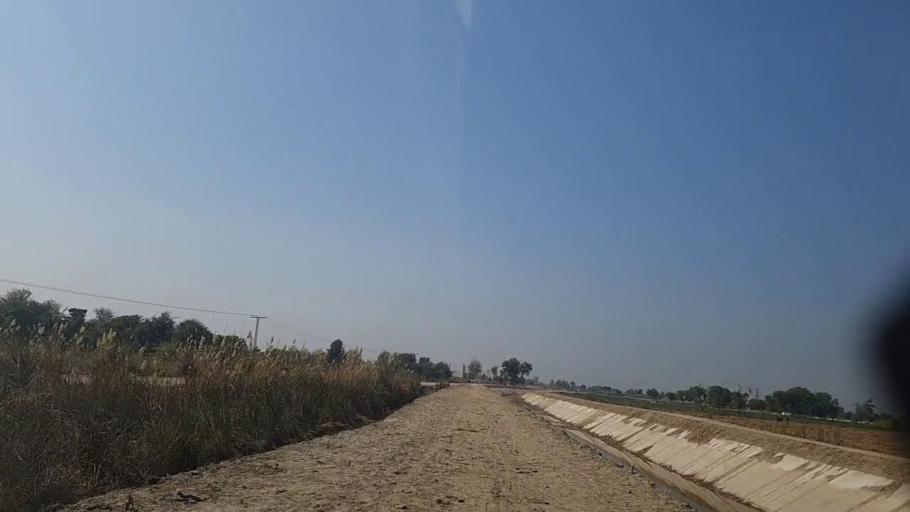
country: PK
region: Sindh
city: Sakrand
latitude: 26.1462
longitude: 68.3381
